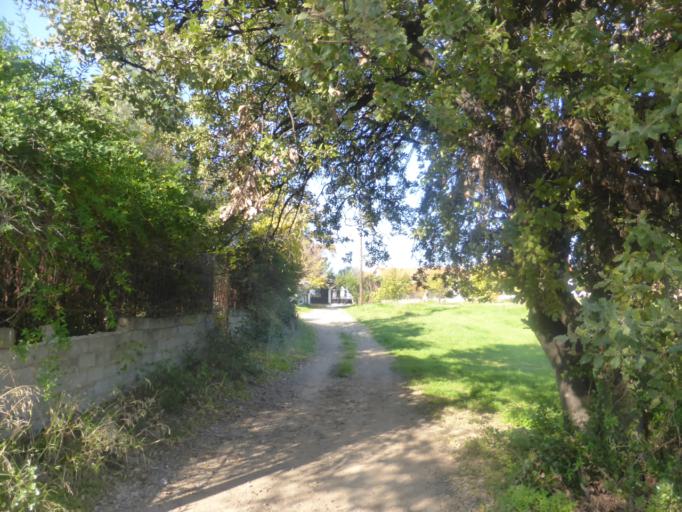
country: GR
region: Attica
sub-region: Nomarchia Anatolikis Attikis
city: Kalamos
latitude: 38.3053
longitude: 23.8503
